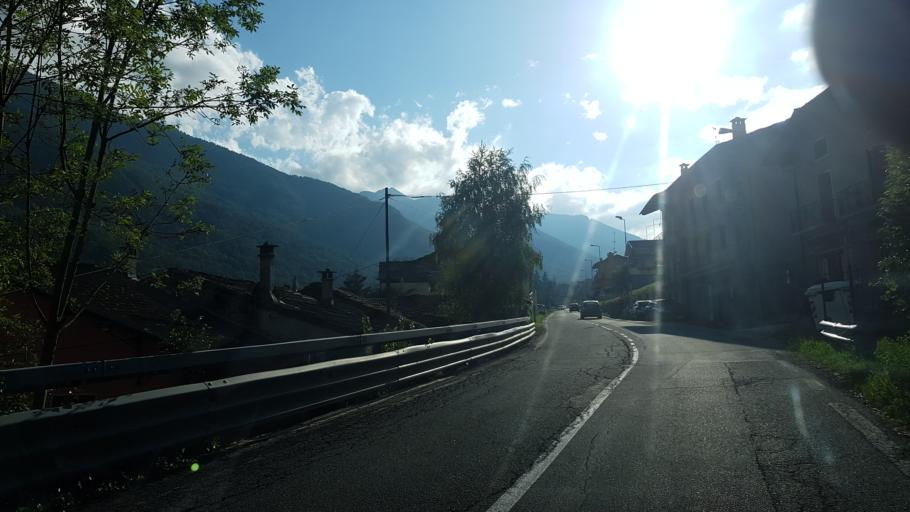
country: IT
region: Piedmont
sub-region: Provincia di Cuneo
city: Sampeyre
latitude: 44.5779
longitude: 7.2038
